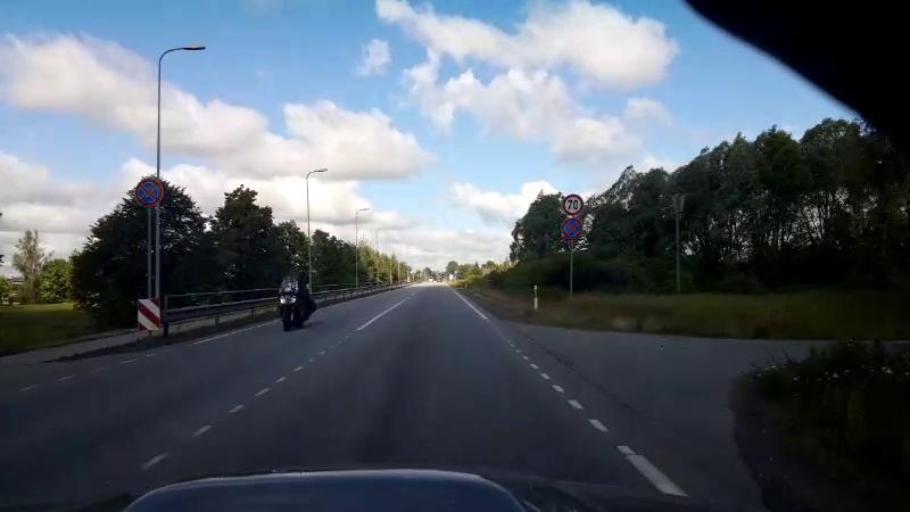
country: LV
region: Bauskas Rajons
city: Bauska
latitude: 56.4040
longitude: 24.2129
